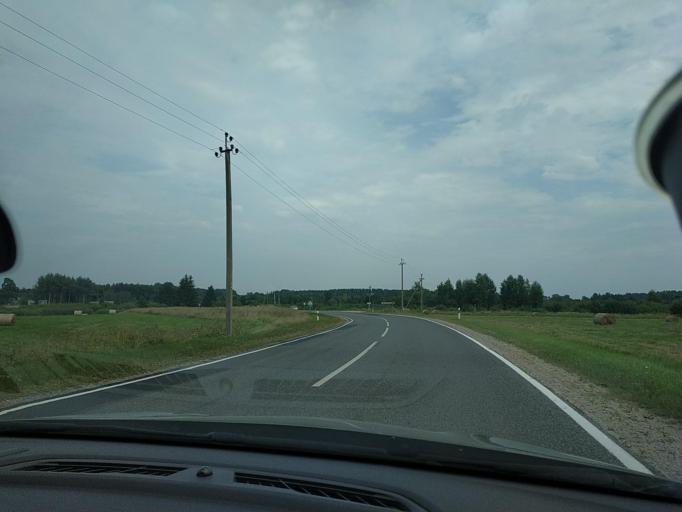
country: LT
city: Nemencine
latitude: 54.8639
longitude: 25.3302
